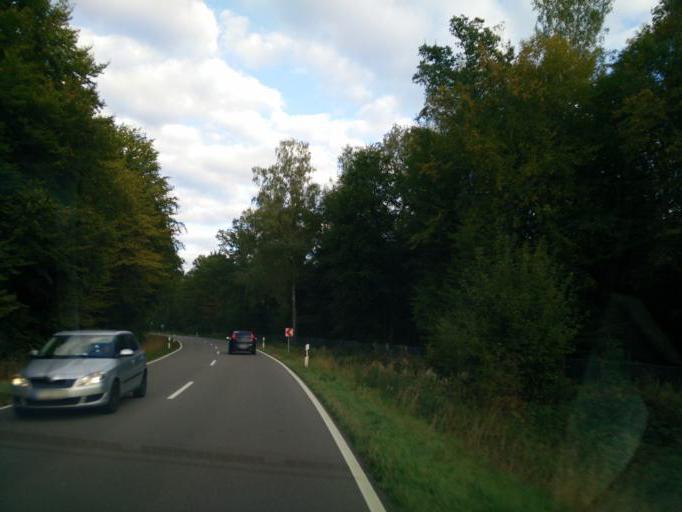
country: DE
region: Baden-Wuerttemberg
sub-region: Tuebingen Region
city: Dettenhausen
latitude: 48.5900
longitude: 9.0770
